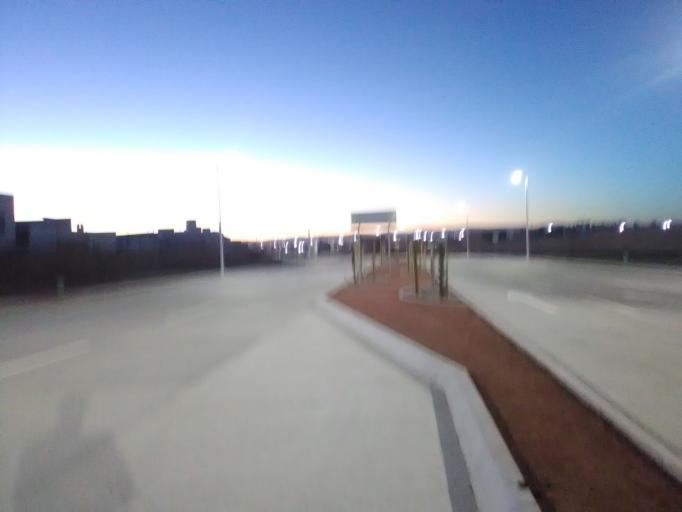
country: MX
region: Durango
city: Victoria de Durango
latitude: 23.9996
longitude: -104.6310
